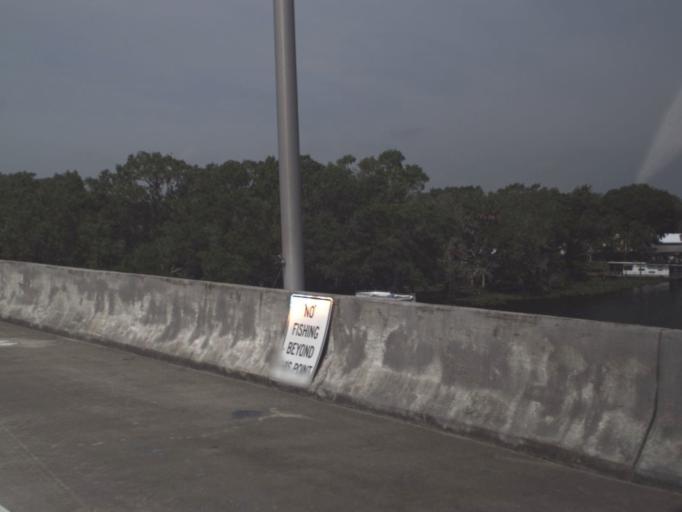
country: US
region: Florida
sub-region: Lake County
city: Astor
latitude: 29.1676
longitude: -81.5228
